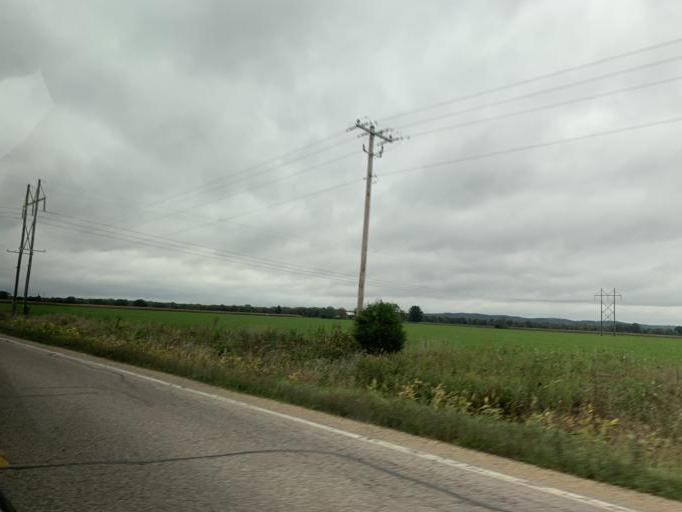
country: US
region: Wisconsin
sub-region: Sauk County
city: Spring Green
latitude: 43.1900
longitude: -90.0451
